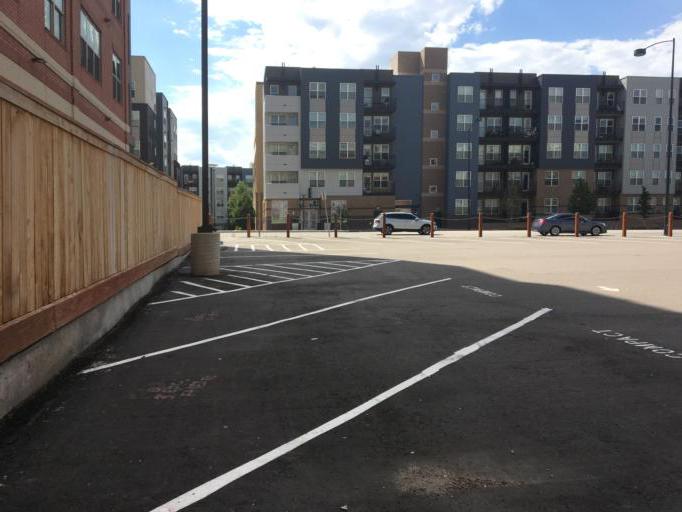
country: US
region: Colorado
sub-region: Denver County
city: Denver
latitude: 39.6954
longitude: -104.9870
